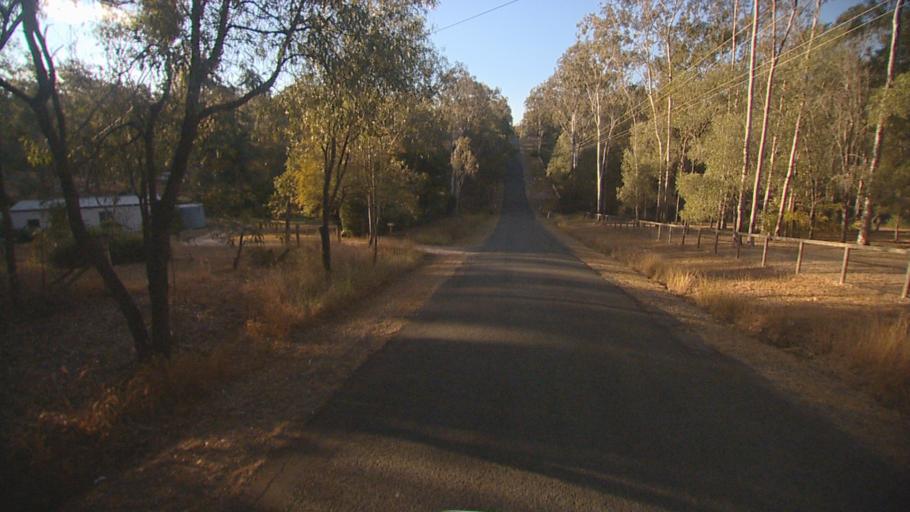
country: AU
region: Queensland
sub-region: Logan
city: Cedar Vale
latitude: -27.8502
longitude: 153.0899
